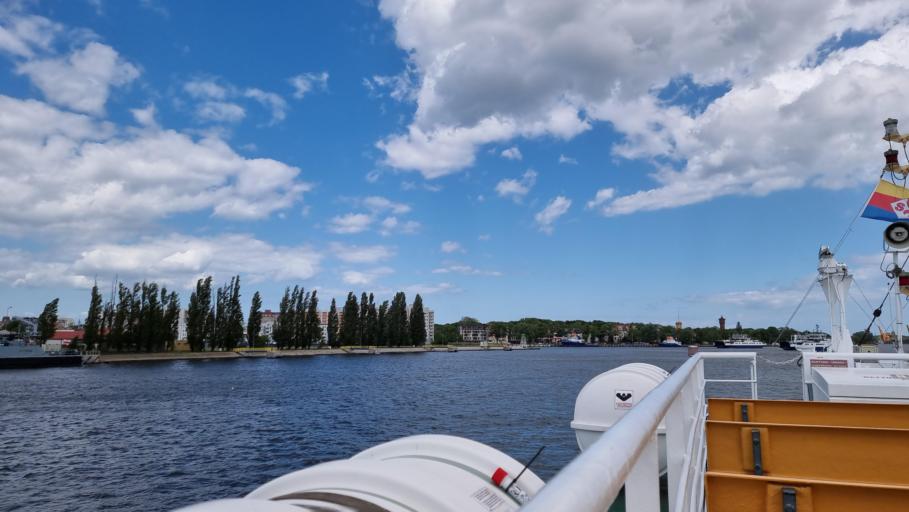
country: PL
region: West Pomeranian Voivodeship
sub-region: Swinoujscie
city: Swinoujscie
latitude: 53.9029
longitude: 14.2565
